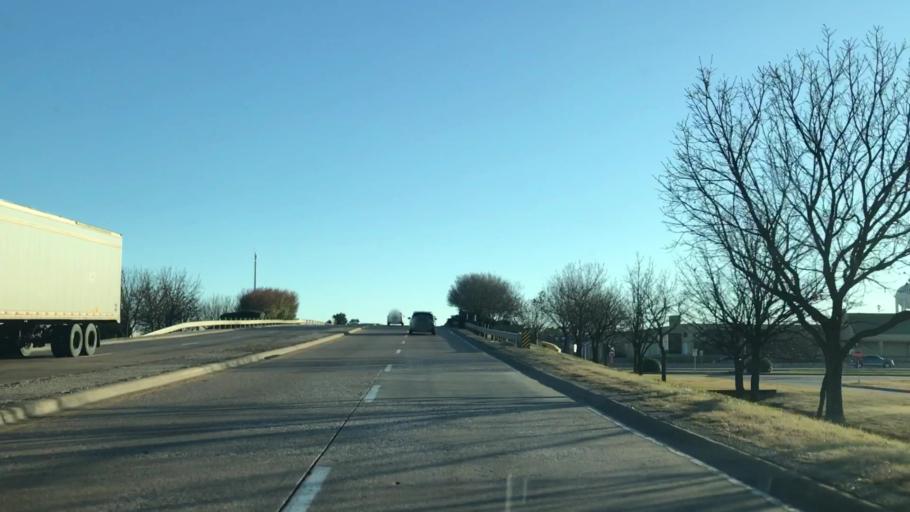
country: US
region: Texas
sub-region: Dallas County
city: Mesquite
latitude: 32.7987
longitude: -96.6683
